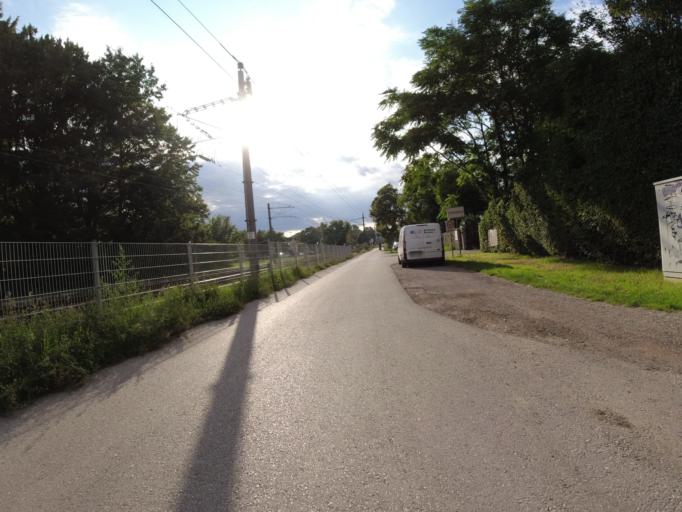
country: AT
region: Lower Austria
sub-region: Politischer Bezirk Baden
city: Pfaffstatten
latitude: 48.0080
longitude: 16.2684
